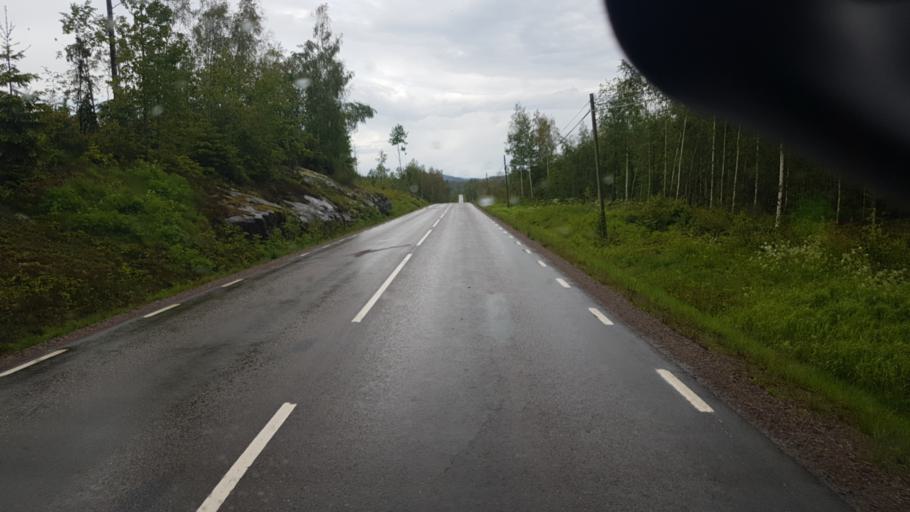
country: SE
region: Vaermland
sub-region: Eda Kommun
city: Amotfors
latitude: 59.7411
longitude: 12.3799
